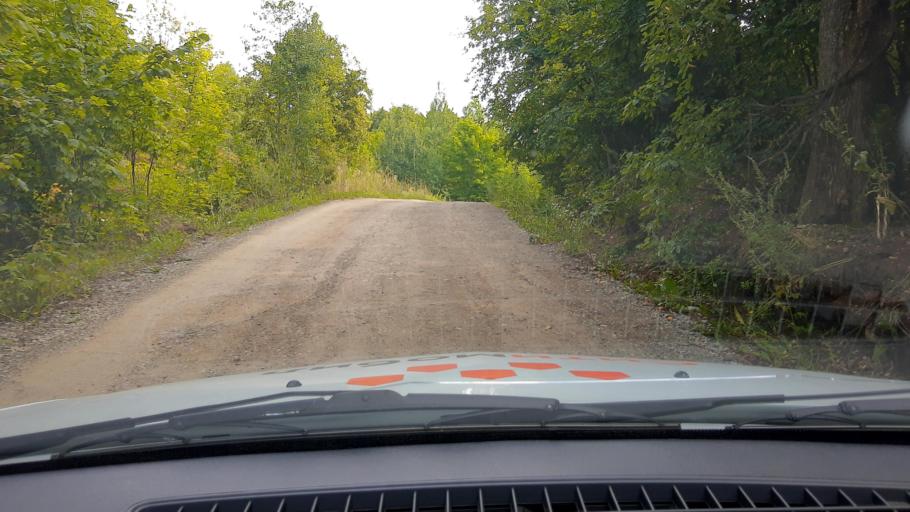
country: RU
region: Bashkortostan
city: Kabakovo
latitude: 54.7043
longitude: 56.1375
